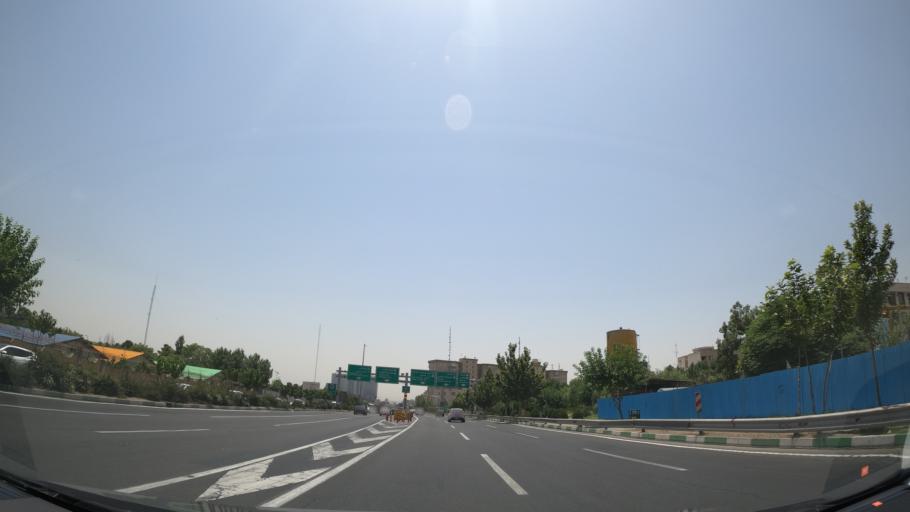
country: IR
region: Tehran
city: Tehran
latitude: 35.7176
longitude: 51.3779
